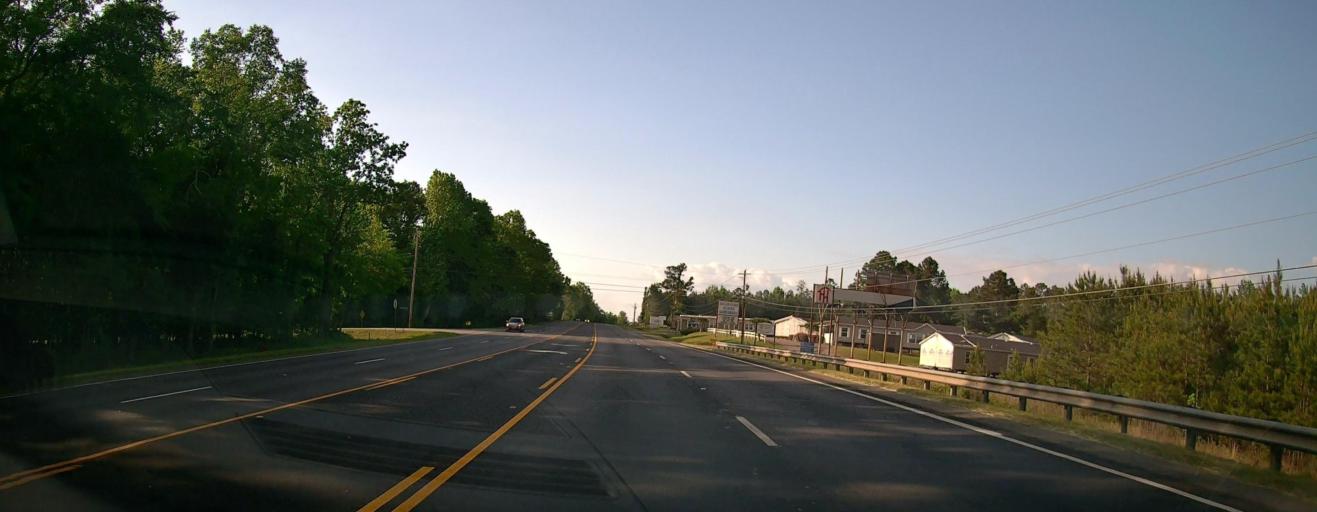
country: US
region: Georgia
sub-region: Baldwin County
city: Milledgeville
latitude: 33.1416
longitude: -83.2710
